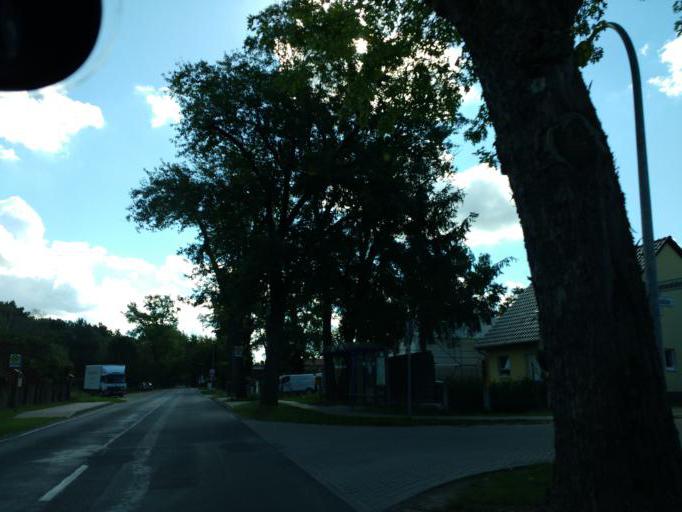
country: DE
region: Brandenburg
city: Mittenwalde
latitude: 52.2178
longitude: 13.5818
